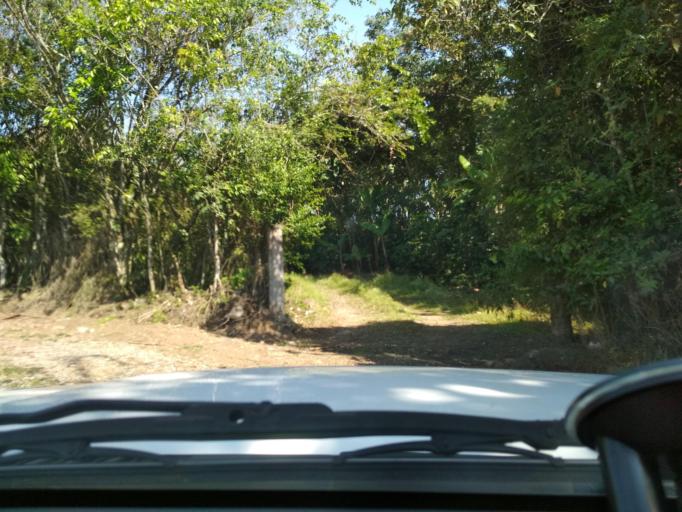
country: MX
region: Veracruz
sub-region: Chocaman
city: San Jose Neria
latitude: 19.0001
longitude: -97.0050
